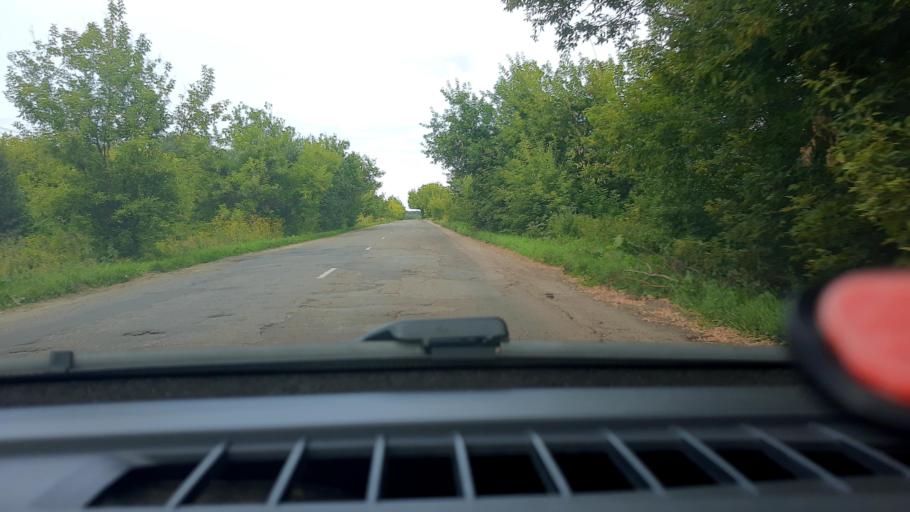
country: RU
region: Nizjnij Novgorod
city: Bogorodsk
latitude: 56.0669
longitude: 43.5889
